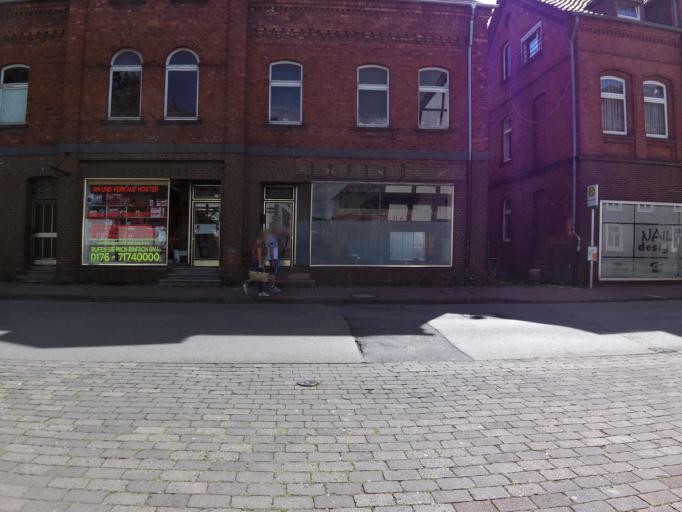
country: DE
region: North Rhine-Westphalia
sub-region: Regierungsbezirk Detmold
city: Hoexter
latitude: 51.7774
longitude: 9.3817
